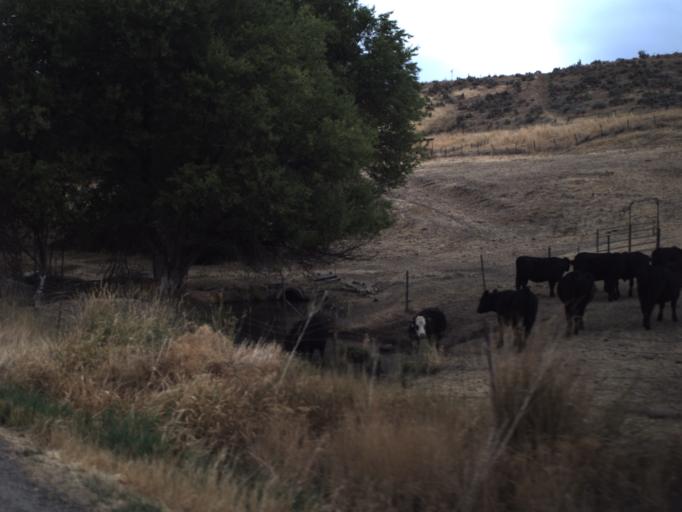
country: US
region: Utah
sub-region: Morgan County
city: Morgan
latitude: 41.0078
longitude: -111.6761
